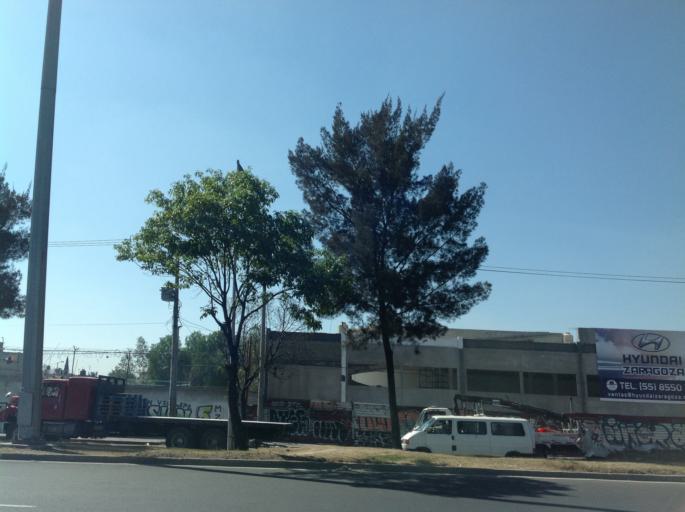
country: MX
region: Mexico
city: Ciudad Nezahualcoyotl
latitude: 19.3886
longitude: -99.0423
